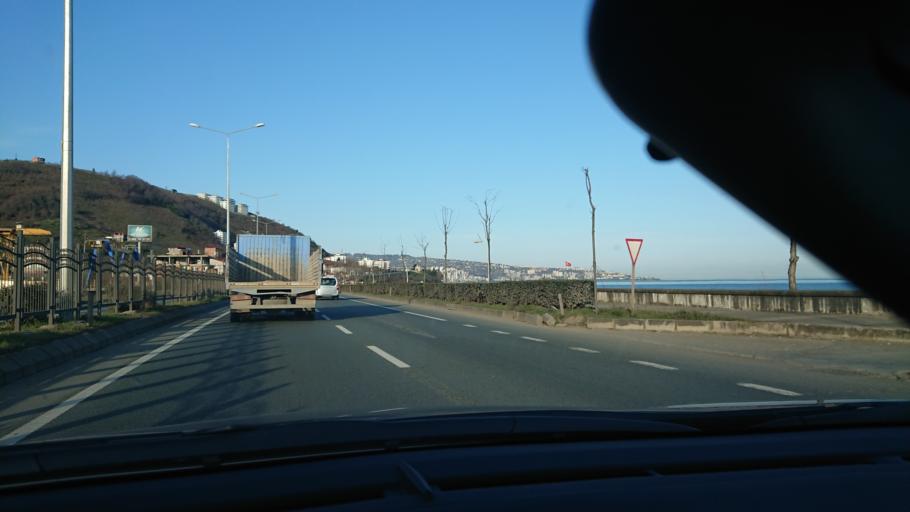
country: TR
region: Trabzon
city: Arsin
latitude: 40.9536
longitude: 39.9079
